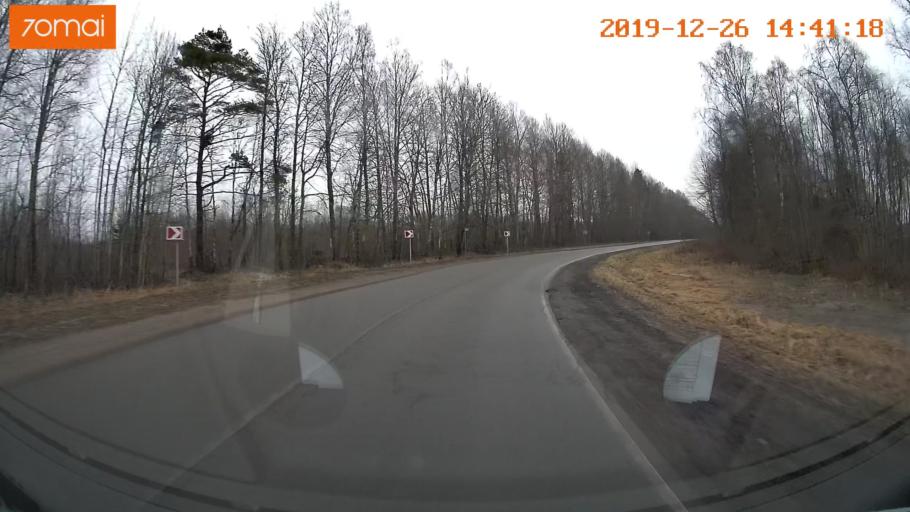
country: RU
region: Jaroslavl
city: Poshekhon'ye
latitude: 58.3724
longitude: 39.0171
